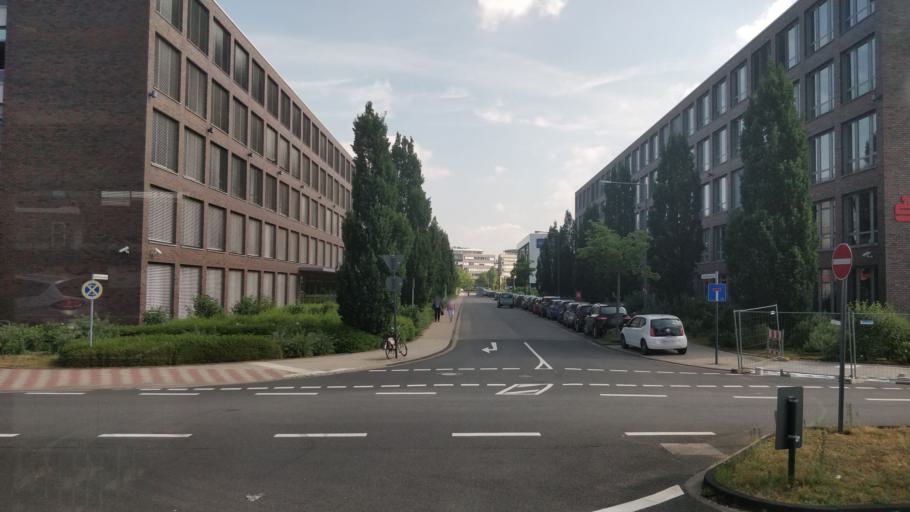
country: DE
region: North Rhine-Westphalia
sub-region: Regierungsbezirk Koln
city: Mengenich
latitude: 50.9845
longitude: 6.8889
